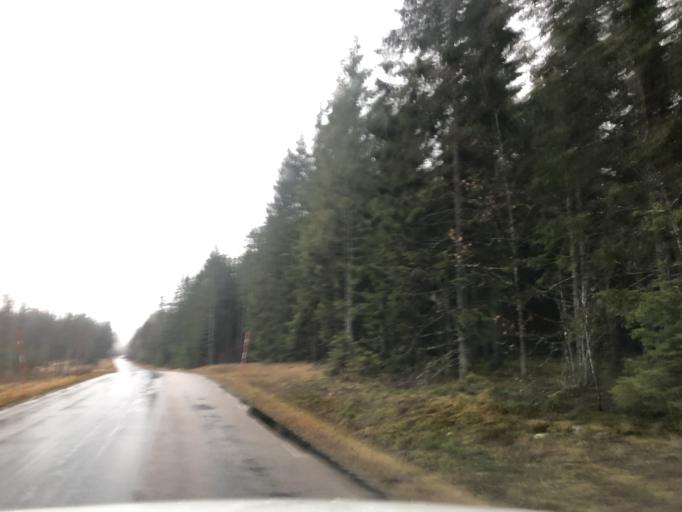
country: SE
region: Vaestra Goetaland
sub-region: Ulricehamns Kommun
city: Ulricehamn
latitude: 57.8409
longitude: 13.5374
